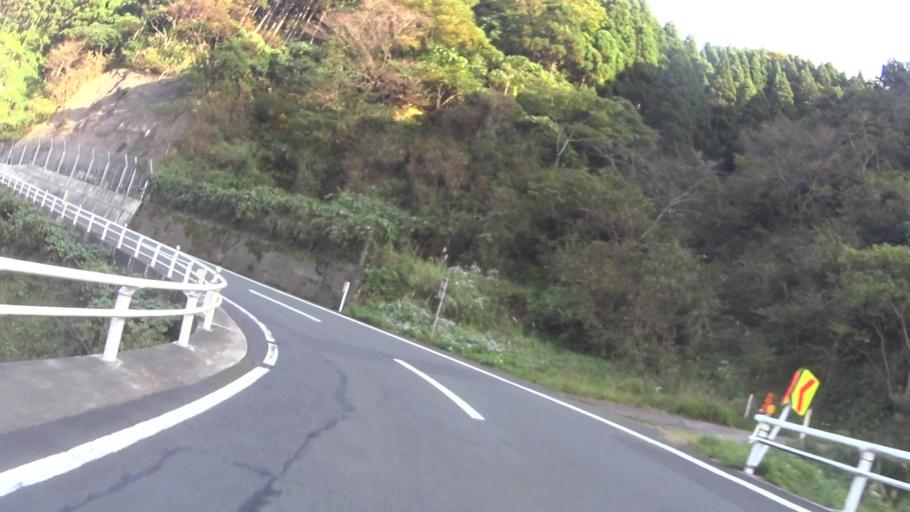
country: JP
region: Kyoto
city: Miyazu
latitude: 35.7624
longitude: 135.2360
